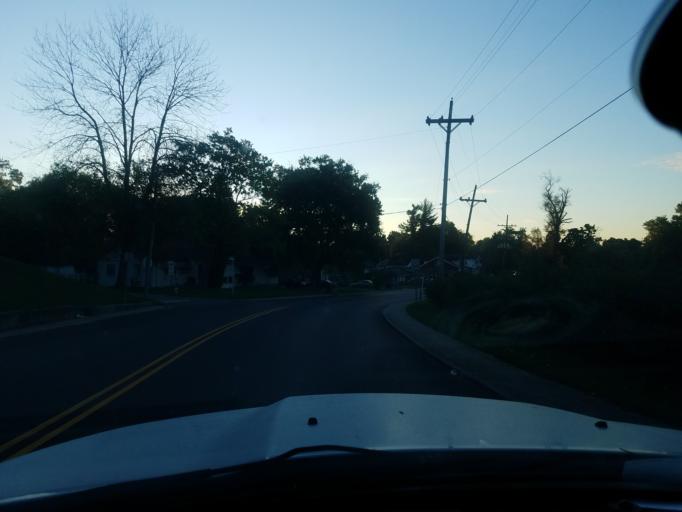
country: US
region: Indiana
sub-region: Floyd County
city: New Albany
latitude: 38.3065
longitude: -85.8092
